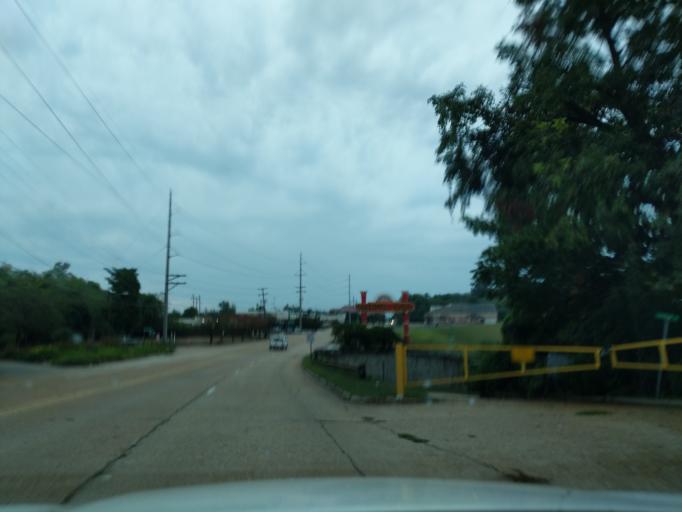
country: US
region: Mississippi
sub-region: Warren County
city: Vicksburg
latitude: 32.3194
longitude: -90.8968
